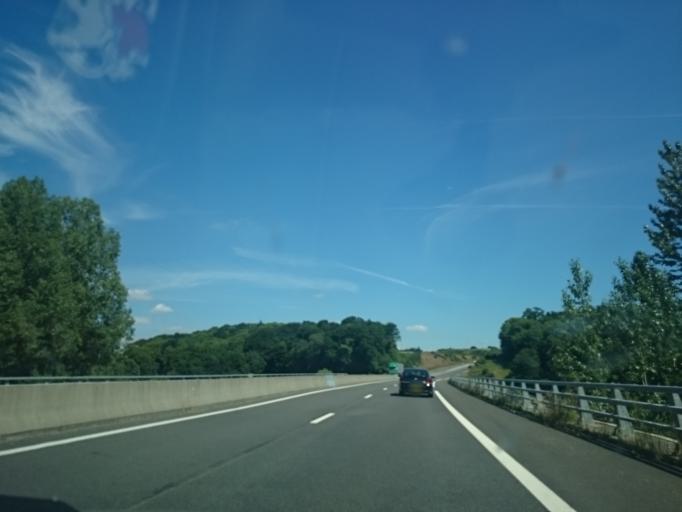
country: FR
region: Brittany
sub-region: Departement des Cotes-d'Armor
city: Gouarec
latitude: 48.2274
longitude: -3.1128
